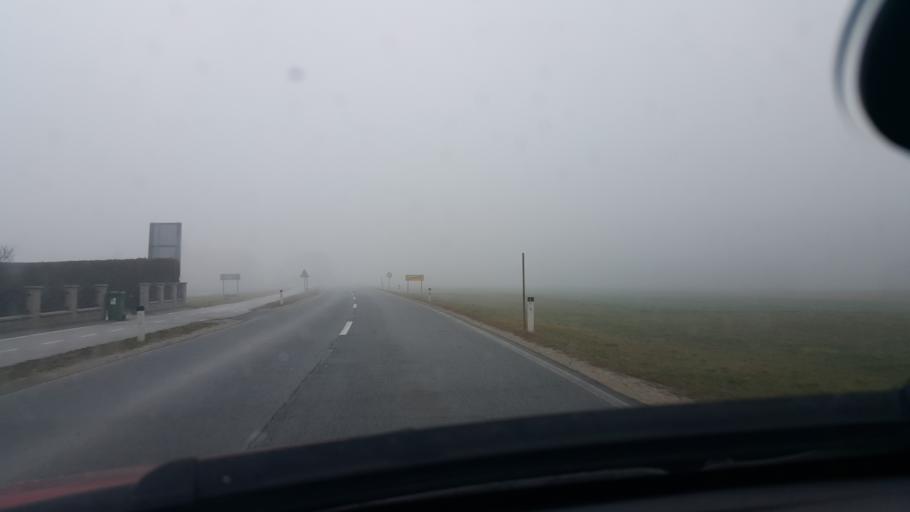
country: SI
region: Podcetrtek
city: Podcetrtek
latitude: 46.1195
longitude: 15.5986
